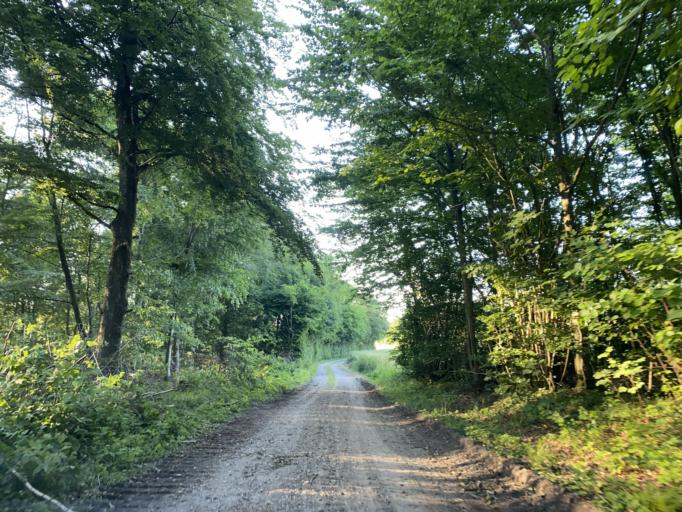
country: DK
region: South Denmark
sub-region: Haderslev Kommune
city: Starup
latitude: 55.1685
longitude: 9.5129
